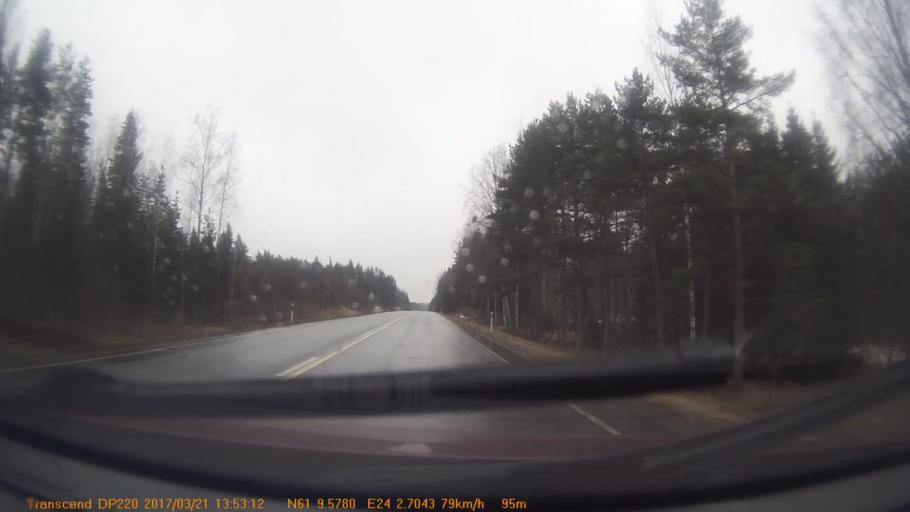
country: FI
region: Haeme
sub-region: Haemeenlinna
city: Kalvola
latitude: 61.1600
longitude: 24.0447
